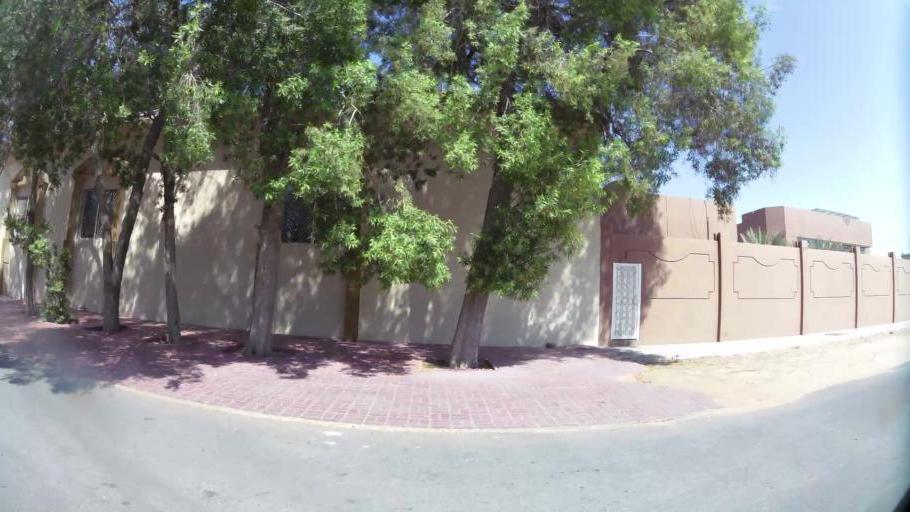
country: AE
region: Ajman
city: Ajman
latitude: 25.4062
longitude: 55.4786
